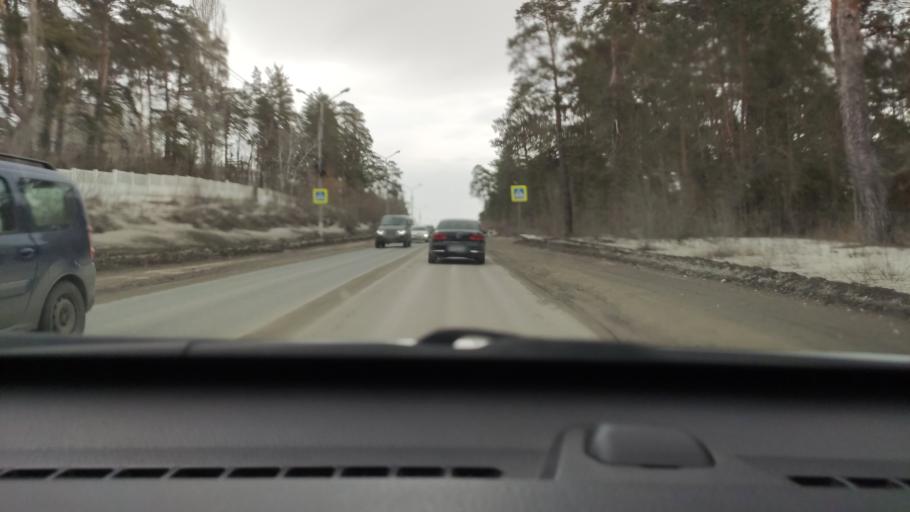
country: RU
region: Samara
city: Tol'yatti
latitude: 53.4772
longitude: 49.3324
